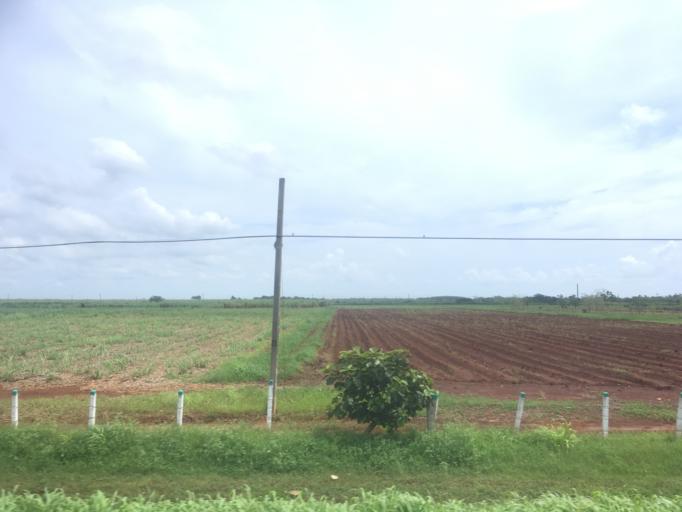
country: CU
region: Matanzas
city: Jovellanos
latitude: 22.7971
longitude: -81.1481
